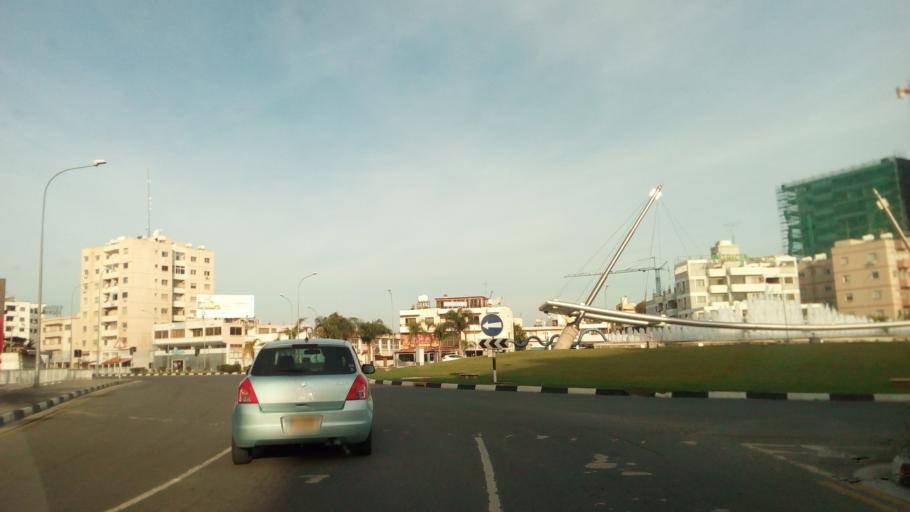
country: CY
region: Larnaka
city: Larnaca
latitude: 34.9298
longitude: 33.6369
